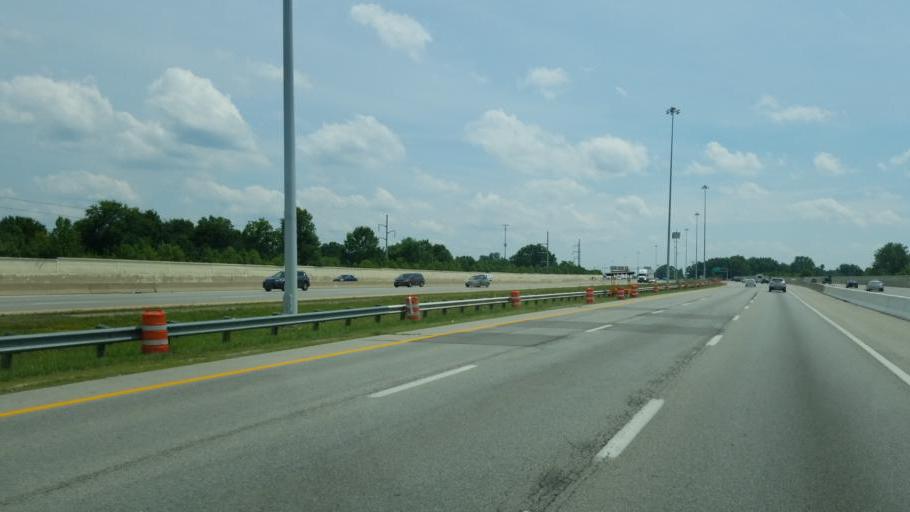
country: US
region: Ohio
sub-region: Franklin County
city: Huber Ridge
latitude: 40.0747
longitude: -82.9079
